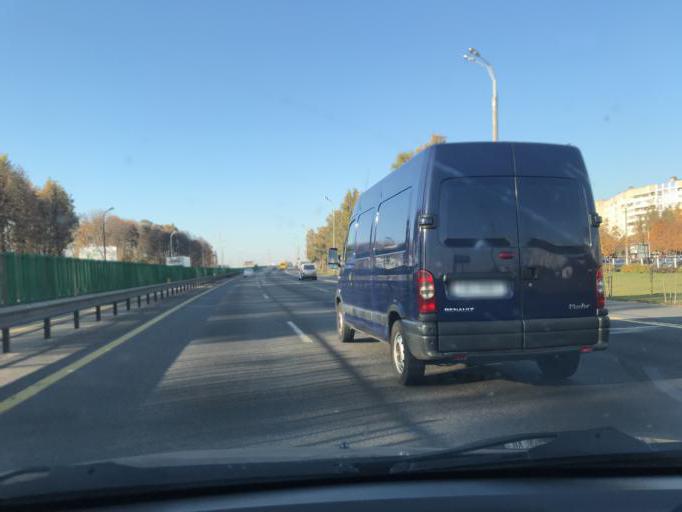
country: BY
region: Minsk
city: Malinovka
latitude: 53.8552
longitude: 27.4306
